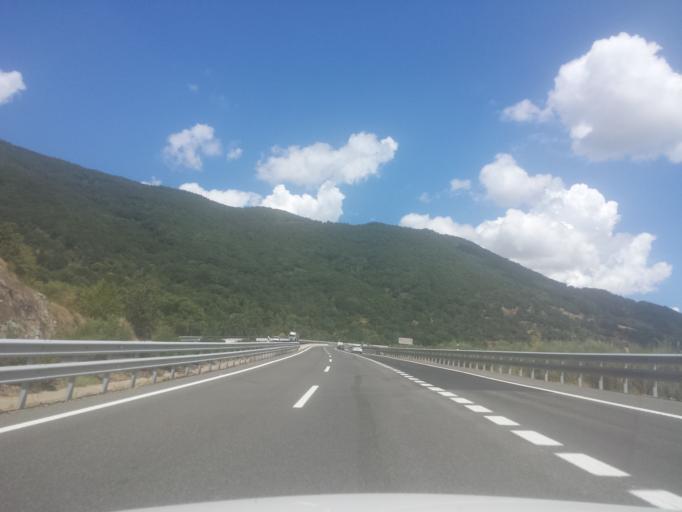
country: ES
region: Extremadura
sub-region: Provincia de Caceres
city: Banos de Montemayor
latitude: 40.3090
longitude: -5.8800
